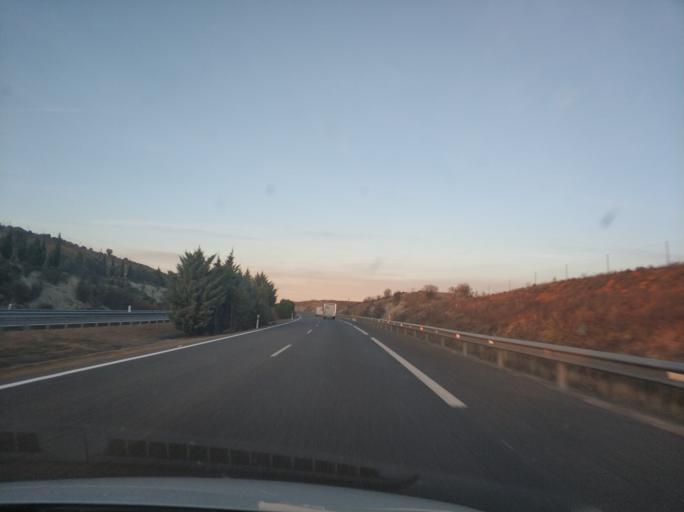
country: ES
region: Castille and Leon
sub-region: Provincia de Palencia
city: Soto de Cerrato
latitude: 41.9554
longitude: -4.4595
